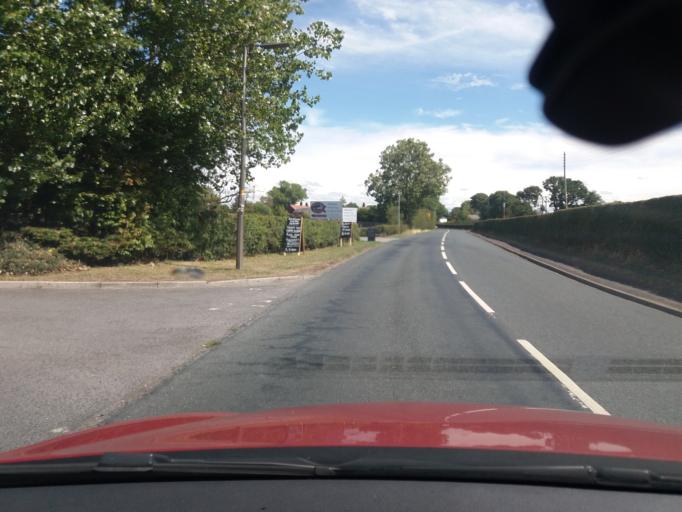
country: GB
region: England
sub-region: Lancashire
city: Euxton
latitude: 53.6623
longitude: -2.7183
